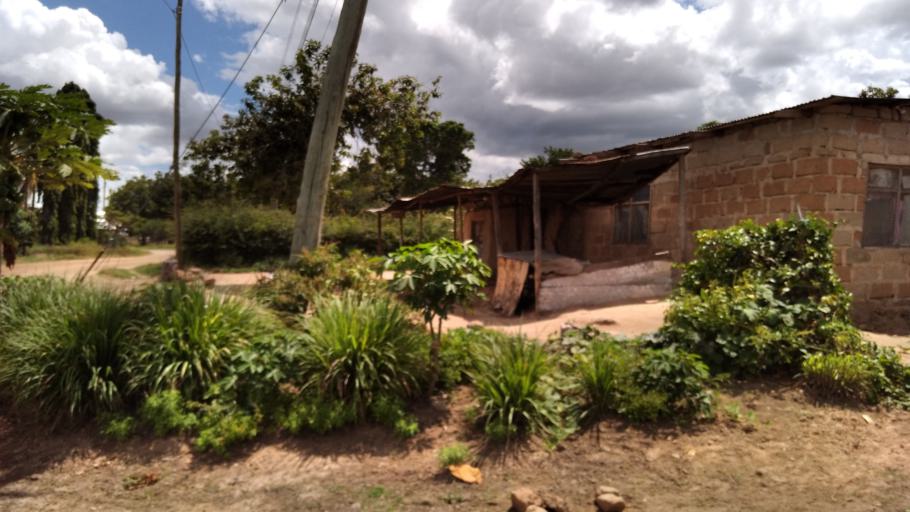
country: TZ
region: Dodoma
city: Dodoma
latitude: -6.1630
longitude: 35.7344
